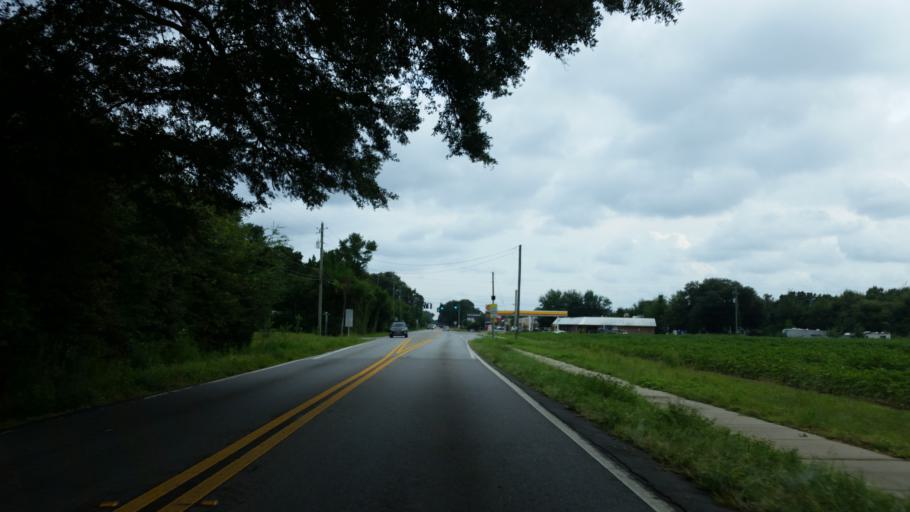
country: US
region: Florida
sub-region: Santa Rosa County
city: Pace
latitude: 30.6162
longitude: -87.1486
